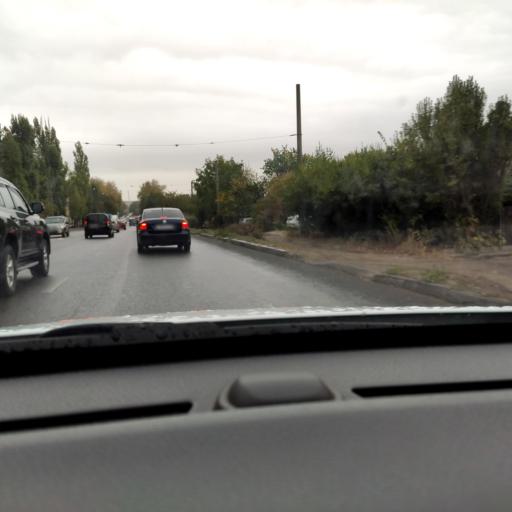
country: RU
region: Voronezj
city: Voronezh
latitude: 51.6951
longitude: 39.1989
